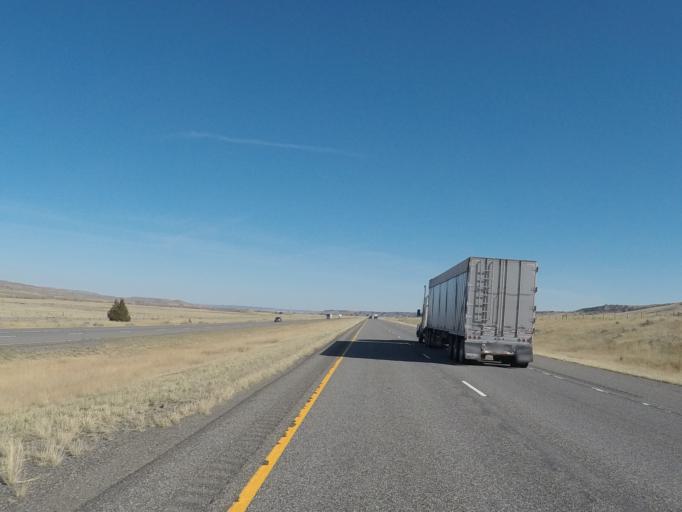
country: US
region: Montana
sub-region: Sweet Grass County
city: Big Timber
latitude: 45.7445
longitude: -110.1857
